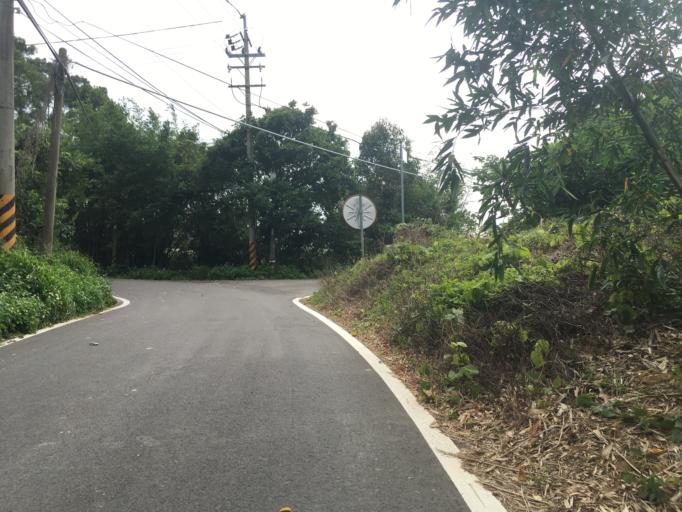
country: TW
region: Taiwan
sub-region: Hsinchu
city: Hsinchu
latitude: 24.7470
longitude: 120.9838
